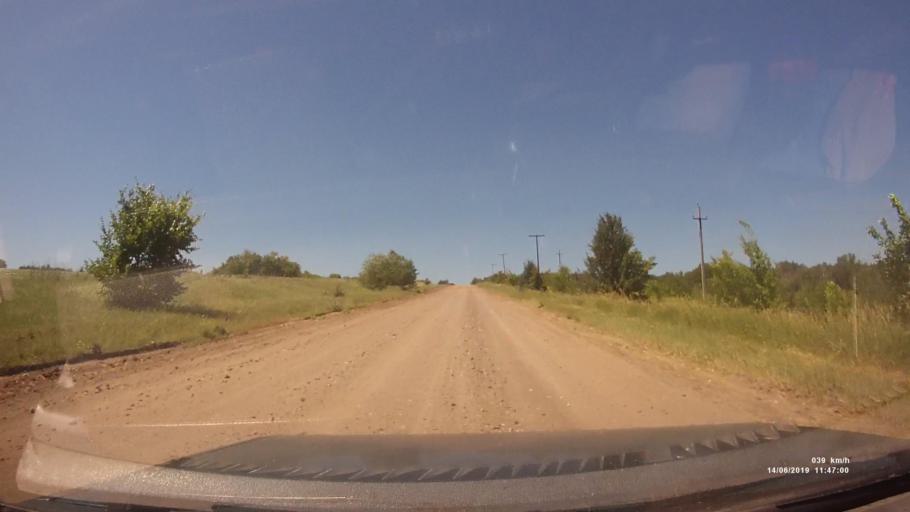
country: RU
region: Rostov
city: Kazanskaya
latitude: 49.8512
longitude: 41.2994
